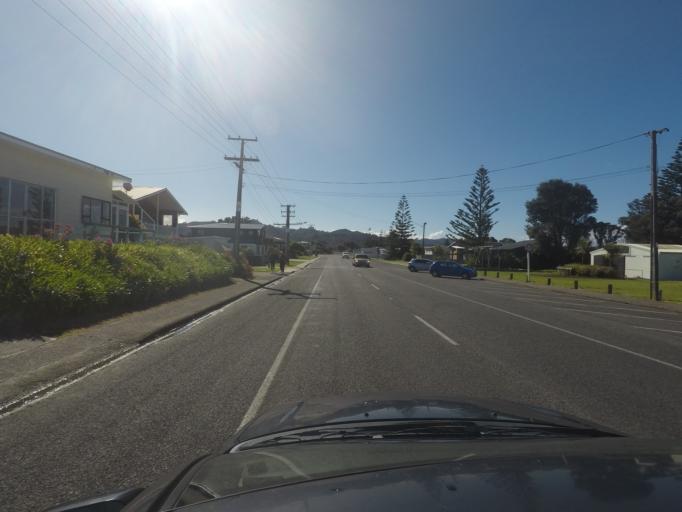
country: NZ
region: Bay of Plenty
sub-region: Western Bay of Plenty District
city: Waihi Beach
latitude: -37.4137
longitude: 175.9467
